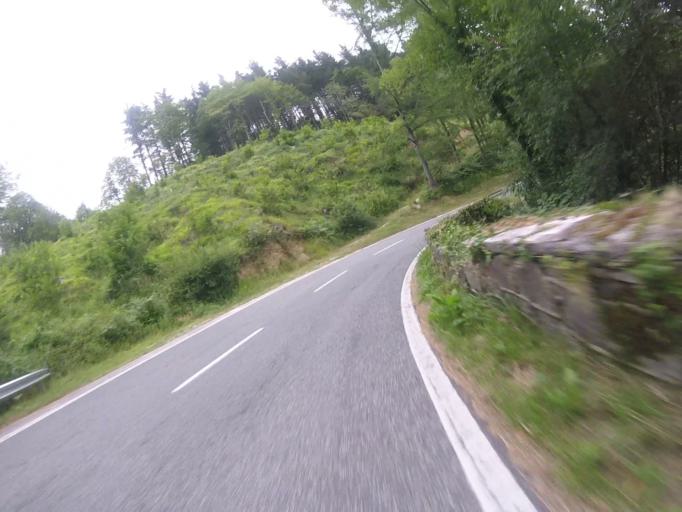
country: ES
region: Navarre
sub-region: Provincia de Navarra
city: Ezkurra
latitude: 43.0849
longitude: -1.8333
